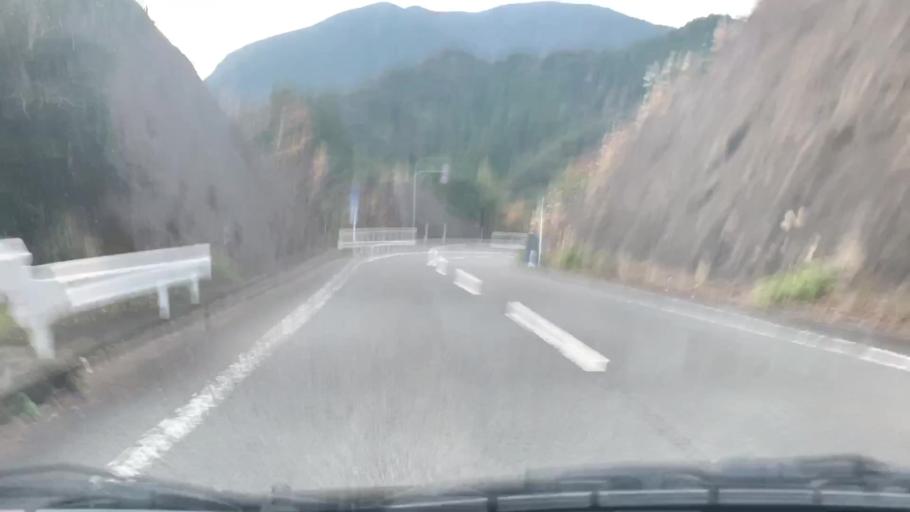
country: JP
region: Nagasaki
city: Omura
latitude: 32.9827
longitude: 130.0370
